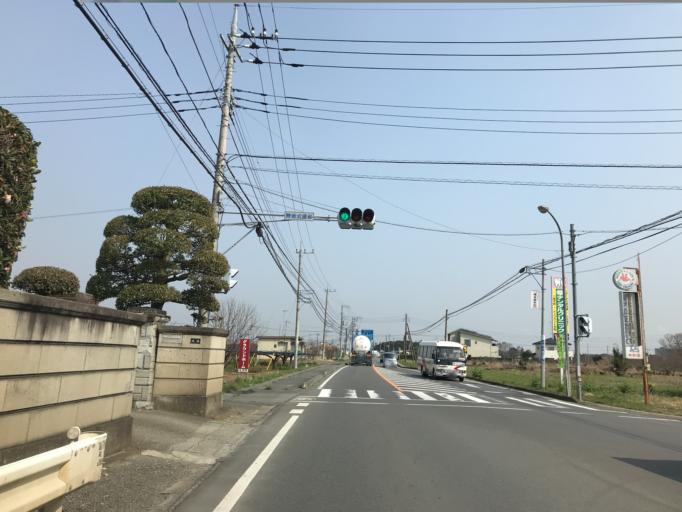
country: JP
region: Ibaraki
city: Tsukuba
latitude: 36.1481
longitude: 140.1620
